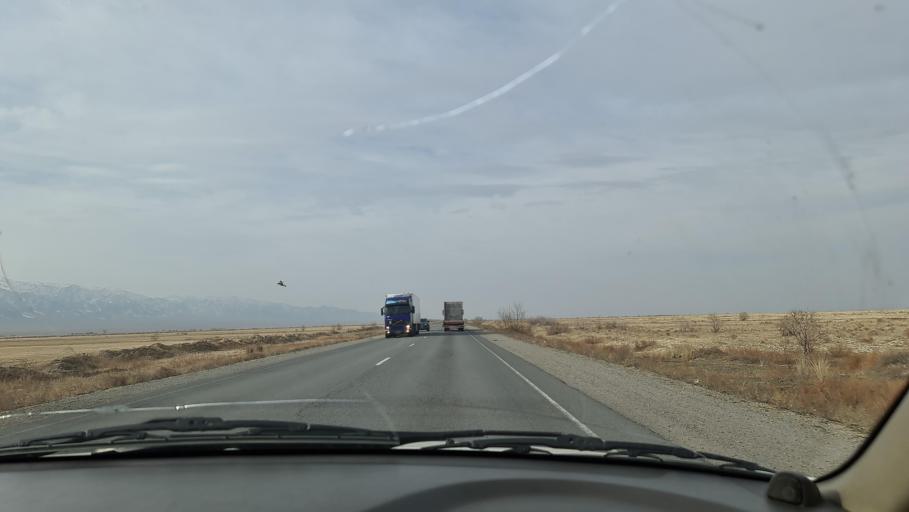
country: KG
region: Chuy
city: Tokmok
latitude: 43.3452
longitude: 75.5201
